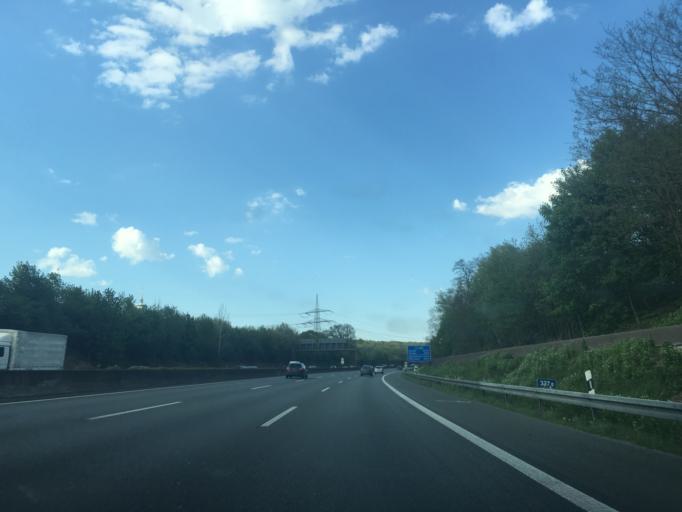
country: DE
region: North Rhine-Westphalia
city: Schwerte
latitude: 51.4485
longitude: 7.5391
